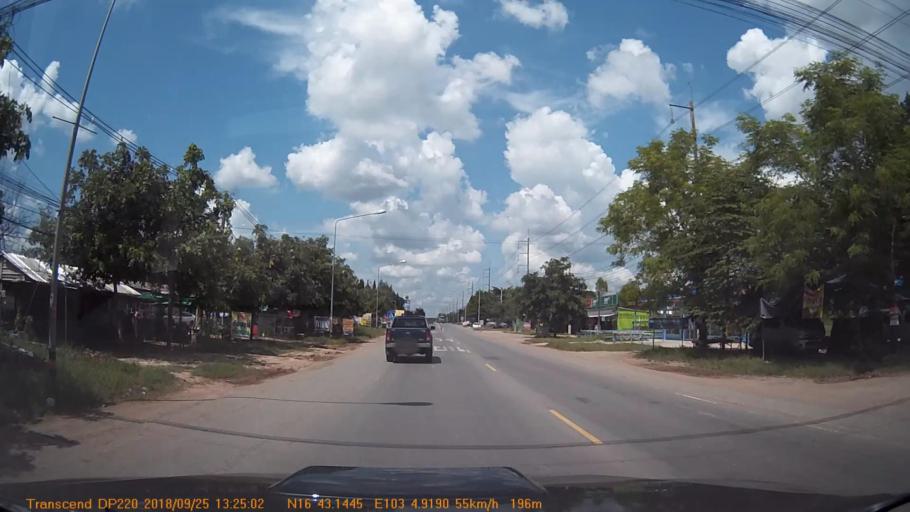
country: TH
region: Khon Kaen
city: Kranuan
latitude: 16.7191
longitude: 103.0820
